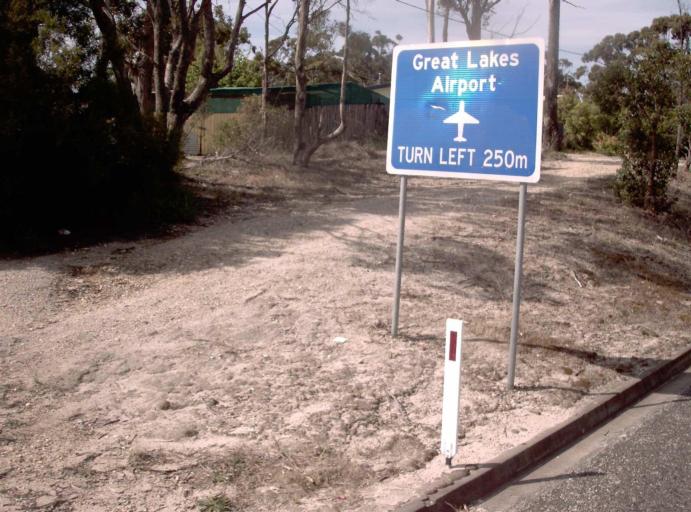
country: AU
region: Victoria
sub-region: East Gippsland
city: Lakes Entrance
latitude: -37.8633
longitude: 148.0243
